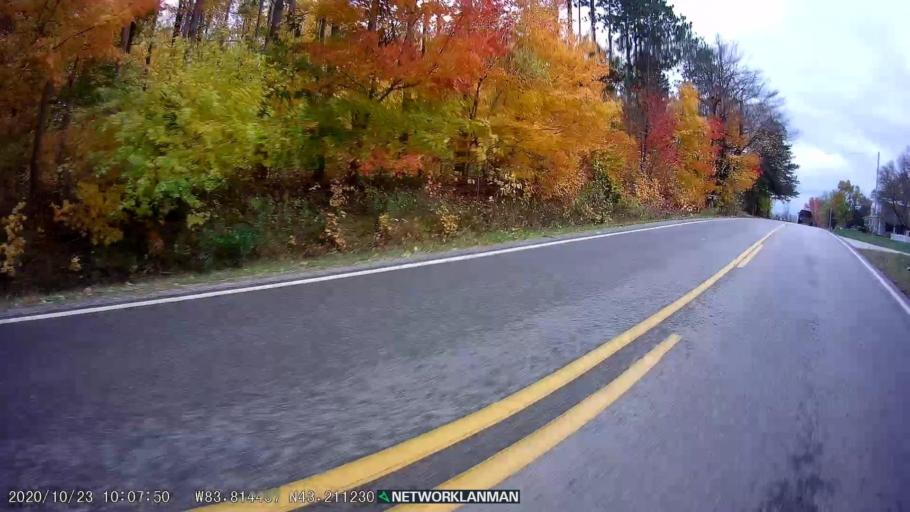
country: US
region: Michigan
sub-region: Saginaw County
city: Birch Run
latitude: 43.2109
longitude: -83.8144
